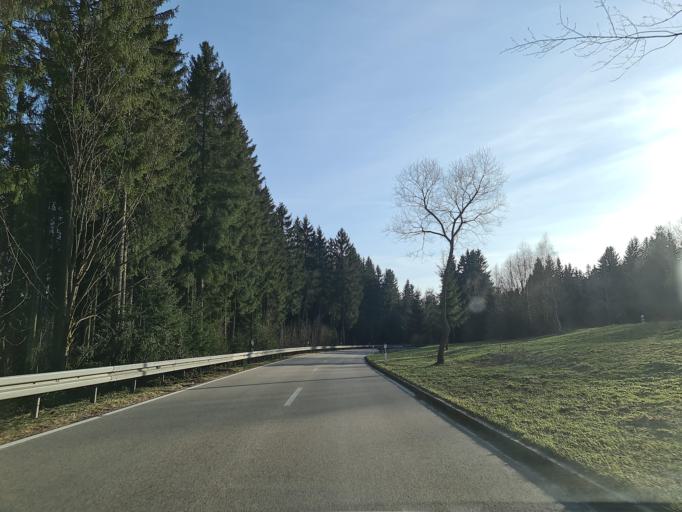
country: DE
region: Saxony
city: Hammerbrucke
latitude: 50.4330
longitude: 12.4063
